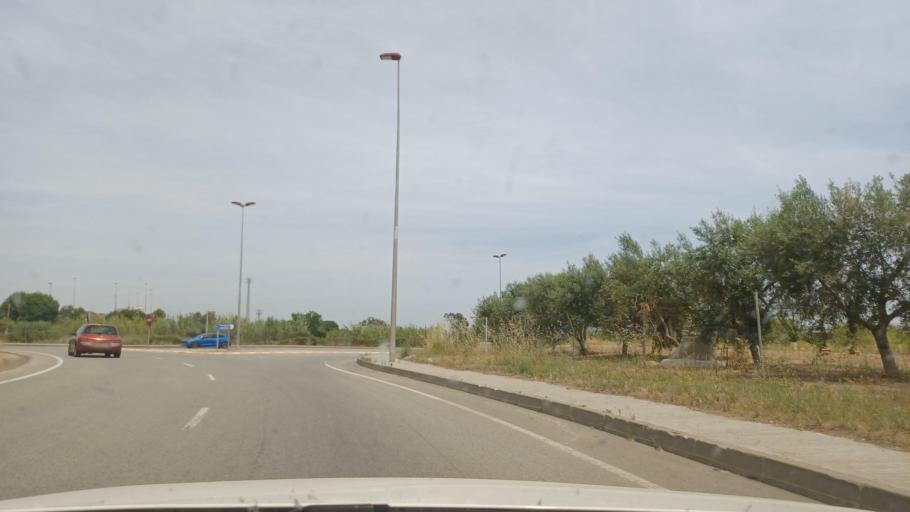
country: ES
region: Catalonia
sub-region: Provincia de Tarragona
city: Vila-seca
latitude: 41.1335
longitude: 1.1429
